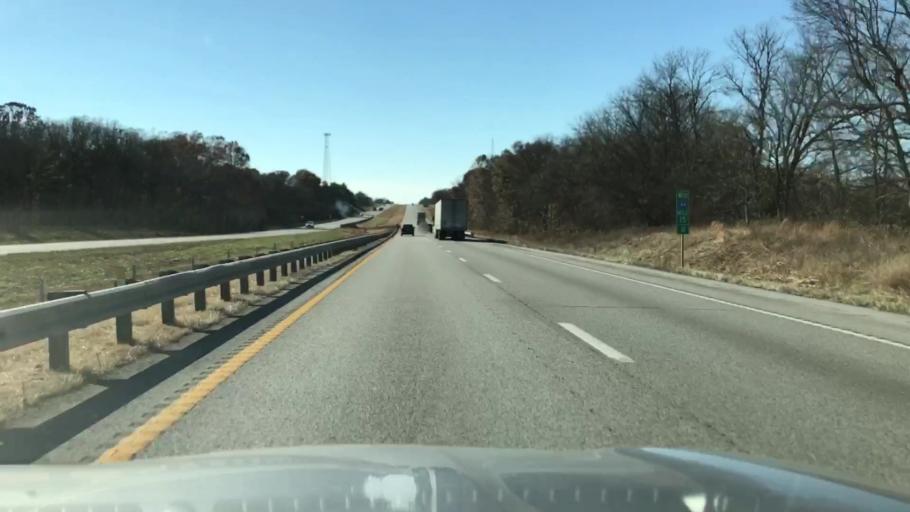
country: US
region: Missouri
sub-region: Jasper County
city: Duenweg
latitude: 37.0792
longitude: -94.3748
